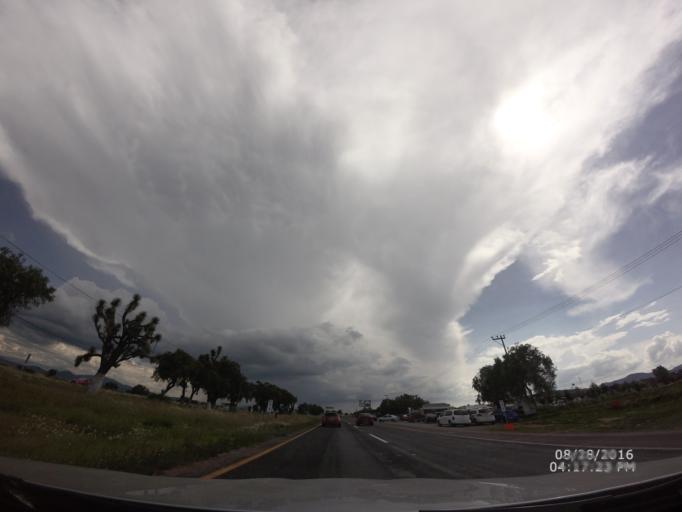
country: MX
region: Hidalgo
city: Zapotlan de Juarez
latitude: 19.9767
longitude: -98.8505
